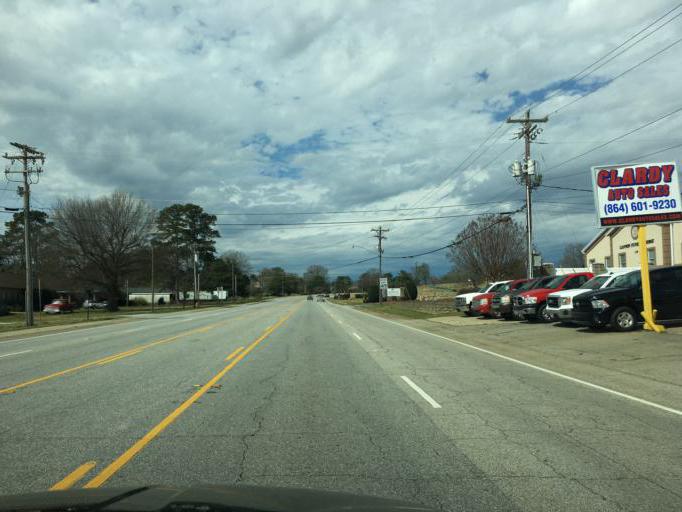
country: US
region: South Carolina
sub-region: Greenville County
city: Fountain Inn
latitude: 34.7018
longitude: -82.2195
